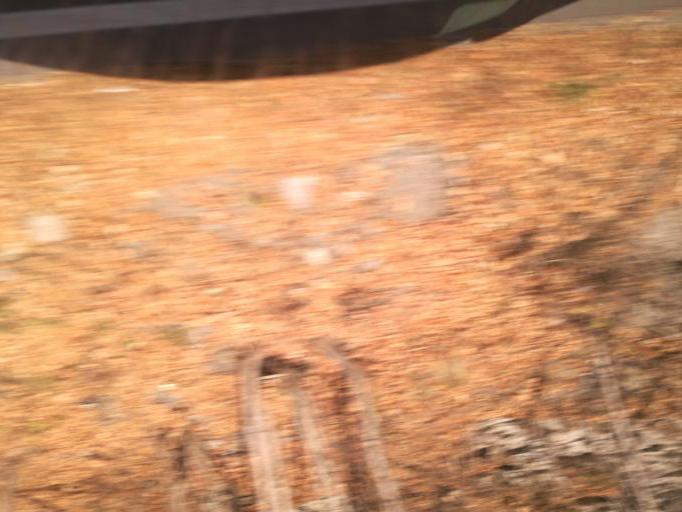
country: RO
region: Prahova
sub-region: Comuna Comarnic
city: Posada
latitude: 45.2970
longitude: 25.5964
